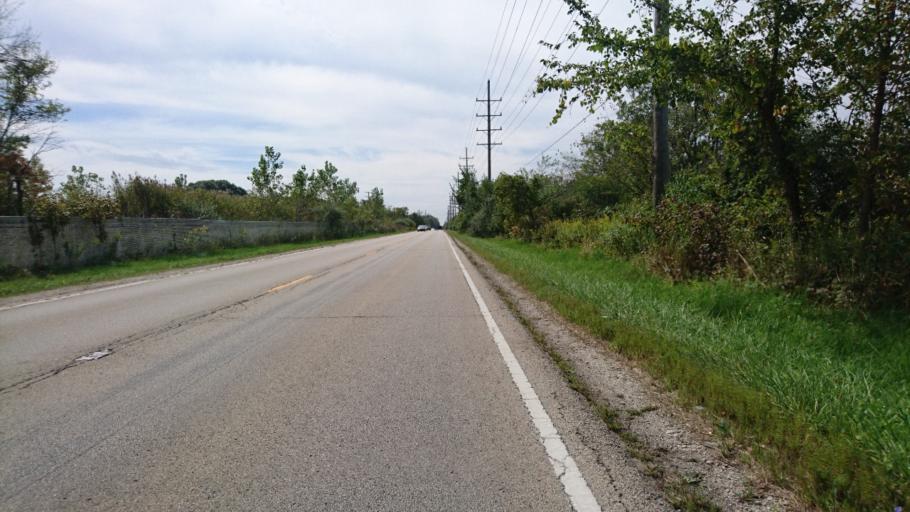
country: US
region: Illinois
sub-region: Will County
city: Wilmington
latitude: 41.2931
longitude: -88.1750
